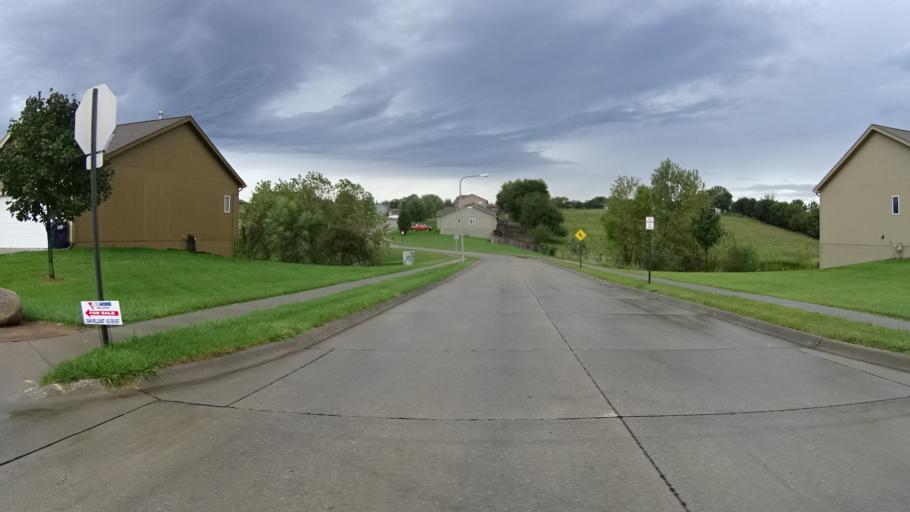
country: US
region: Nebraska
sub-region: Sarpy County
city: Offutt Air Force Base
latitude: 41.1546
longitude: -95.9519
